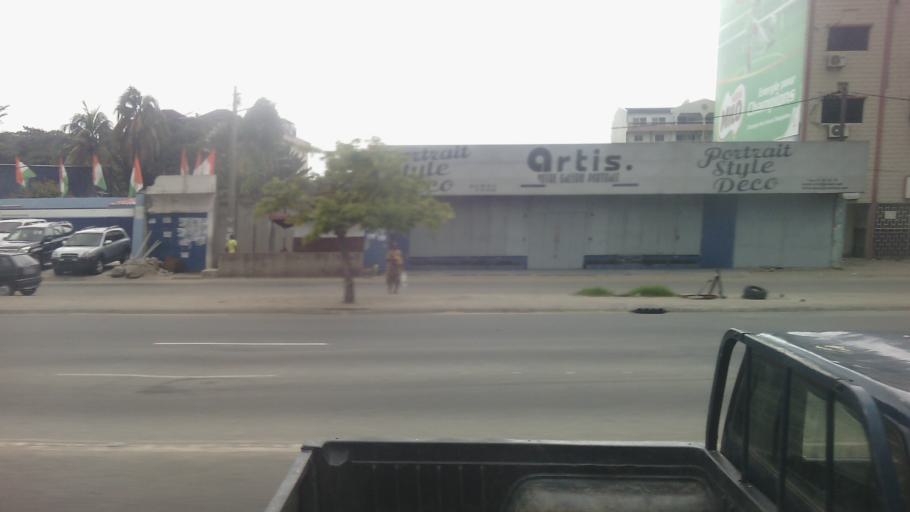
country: CI
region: Lagunes
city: Abidjan
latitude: 5.2927
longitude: -3.9751
